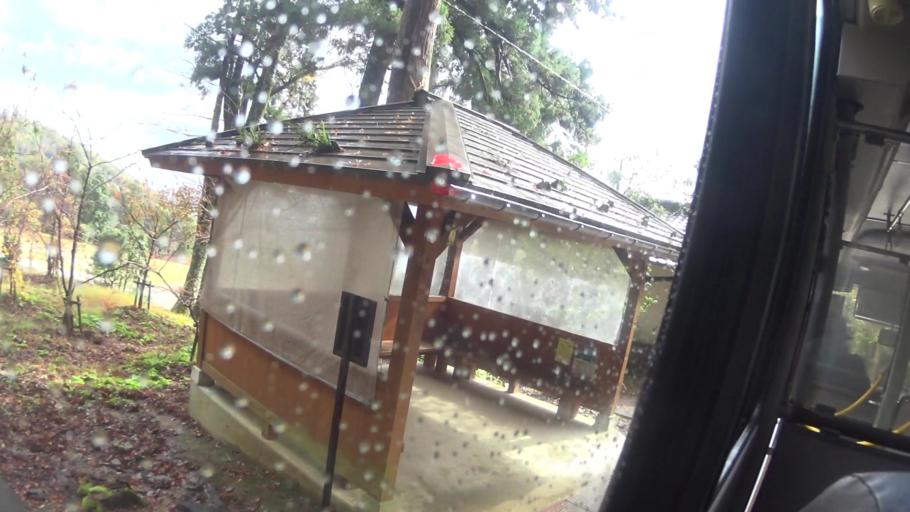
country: JP
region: Kyoto
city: Miyazu
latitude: 35.5941
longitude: 135.1878
